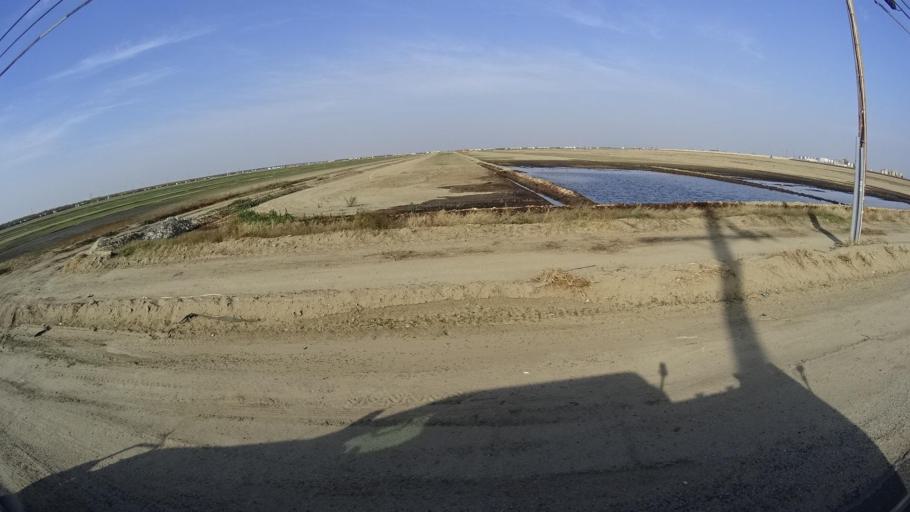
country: US
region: California
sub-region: Kern County
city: Delano
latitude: 35.7760
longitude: -119.2006
